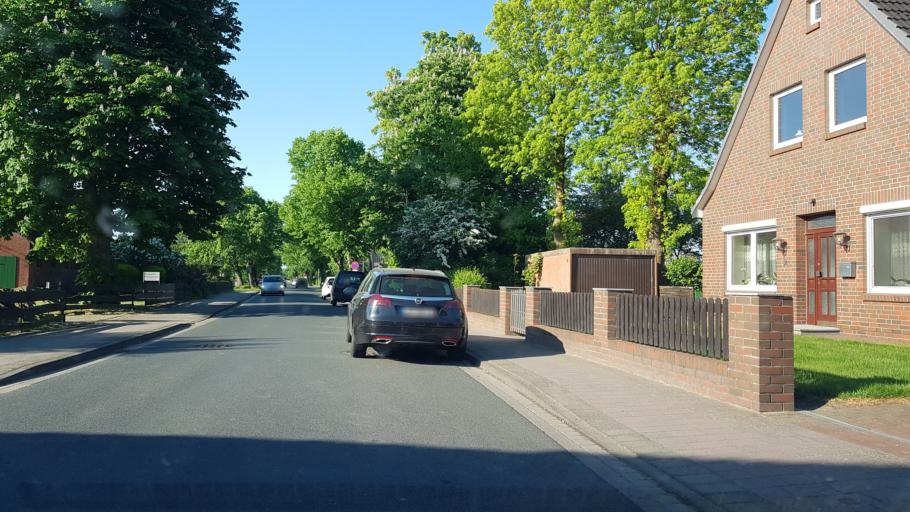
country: DE
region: Lower Saxony
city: Wremen
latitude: 53.6101
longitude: 8.5370
